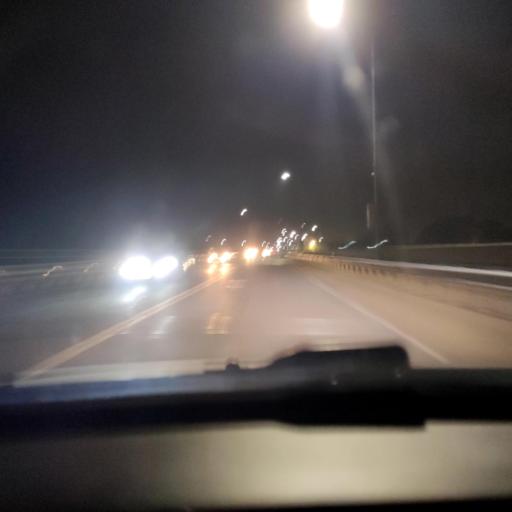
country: RU
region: Voronezj
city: Somovo
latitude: 51.6834
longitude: 39.3478
